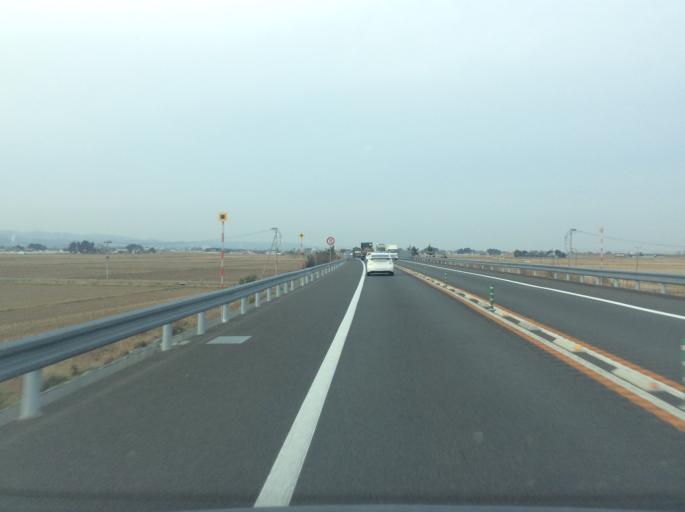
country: JP
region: Miyagi
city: Iwanuma
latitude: 38.0688
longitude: 140.8926
